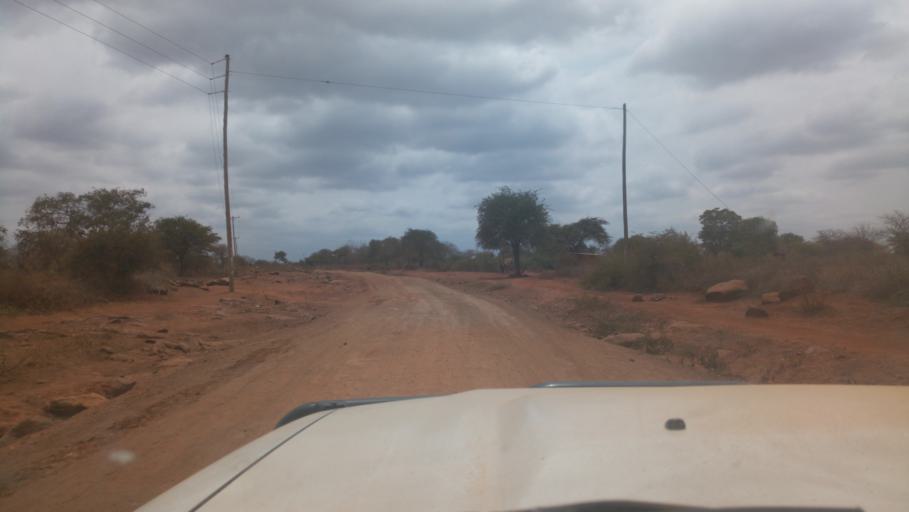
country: KE
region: Makueni
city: Wote
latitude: -1.8214
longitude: 37.9308
